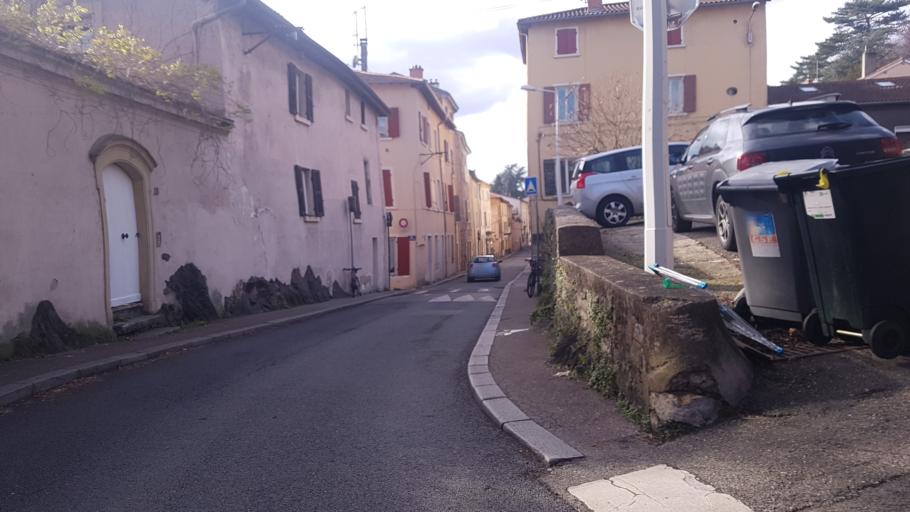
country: FR
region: Rhone-Alpes
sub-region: Departement du Rhone
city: Caluire-et-Cuire
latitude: 45.7990
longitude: 4.8321
